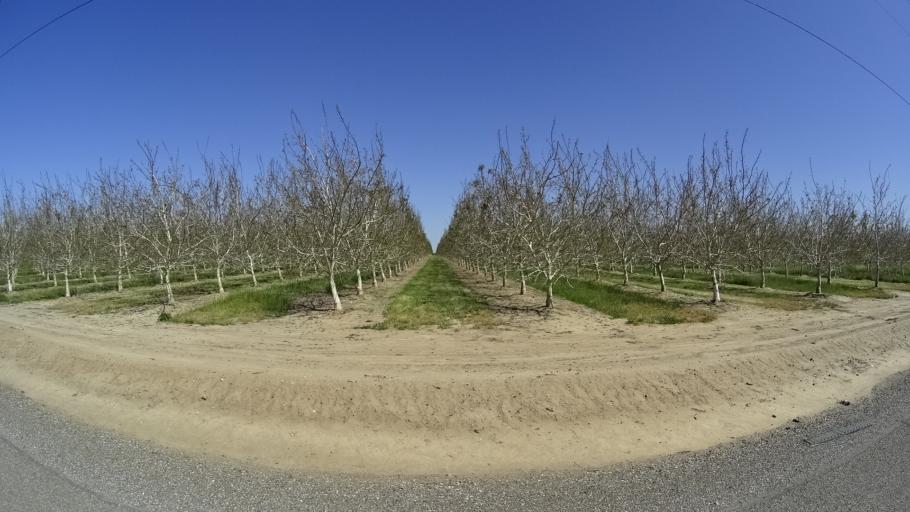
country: US
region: California
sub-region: Glenn County
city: Orland
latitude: 39.7105
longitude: -122.1157
